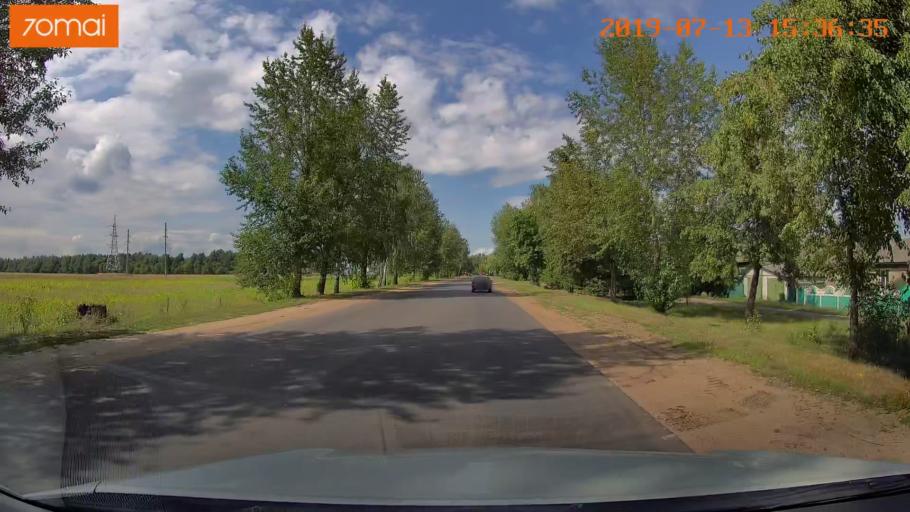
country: BY
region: Mogilev
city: Babruysk
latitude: 53.1328
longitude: 29.1666
